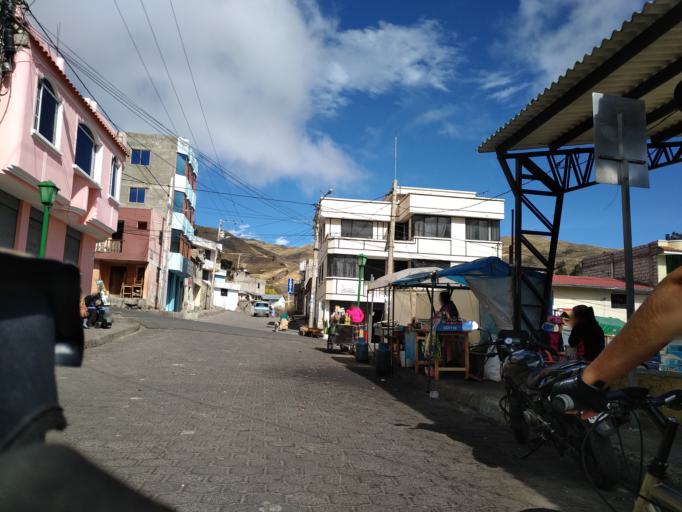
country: EC
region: Cotopaxi
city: Pujili
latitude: -0.9613
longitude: -78.8987
